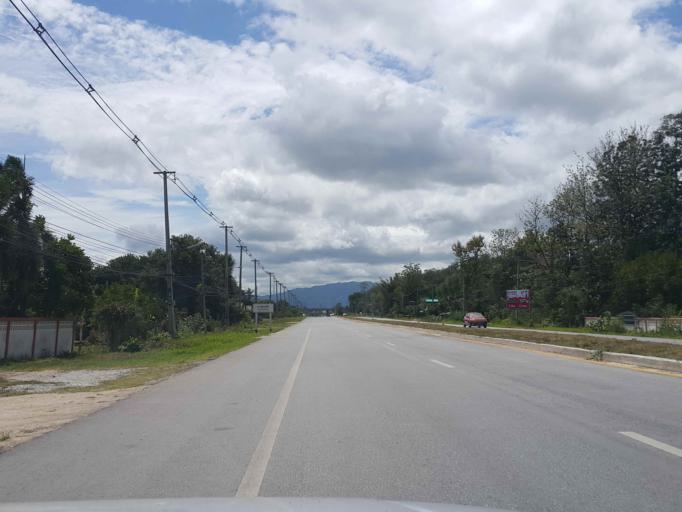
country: TH
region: Tak
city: Tak
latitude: 16.8867
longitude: 99.1801
